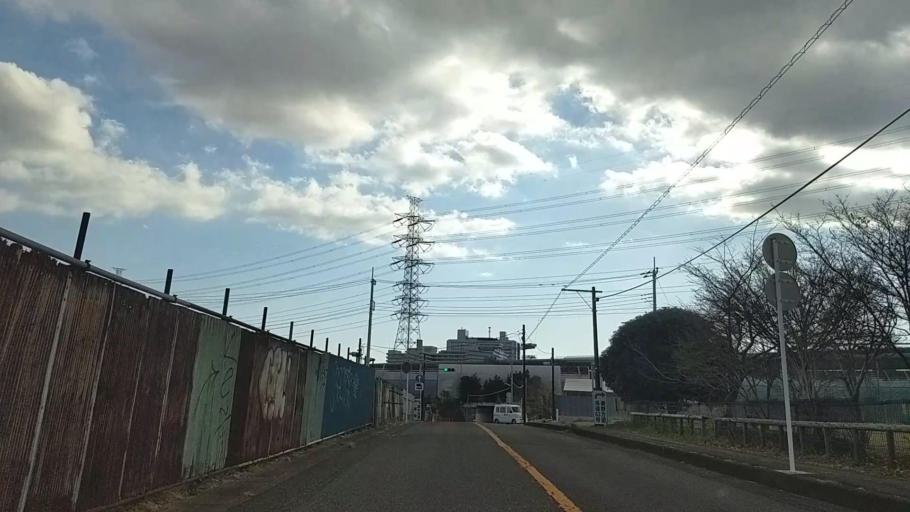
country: JP
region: Kanagawa
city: Isehara
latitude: 35.4140
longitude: 139.3130
